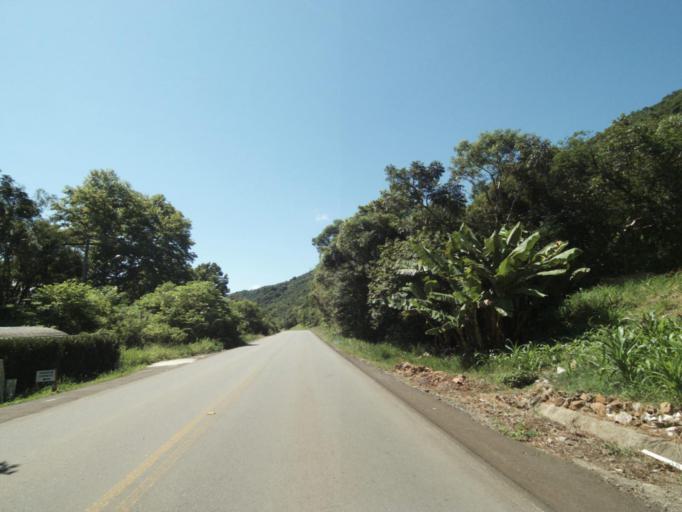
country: BR
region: Rio Grande do Sul
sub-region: Bento Goncalves
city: Bento Goncalves
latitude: -29.0853
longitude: -51.6543
